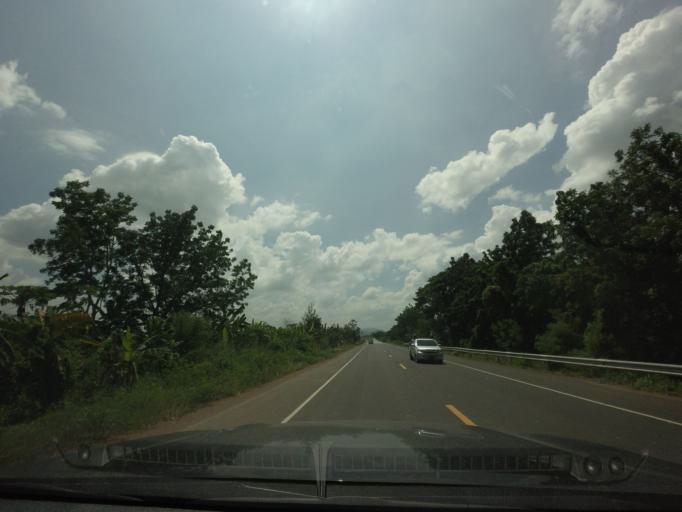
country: TH
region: Phetchabun
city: Phetchabun
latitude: 16.4506
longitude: 101.1135
